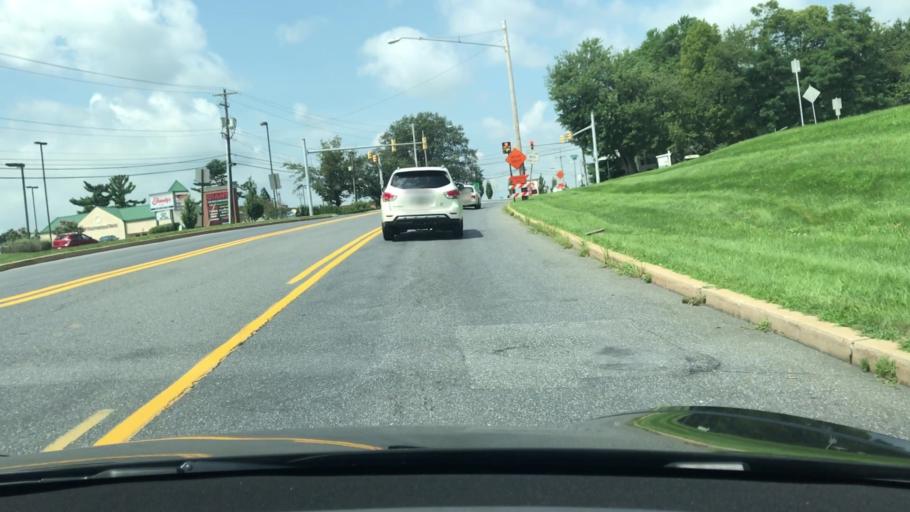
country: US
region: Pennsylvania
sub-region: Lancaster County
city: Mountville
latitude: 40.0547
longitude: -76.3980
